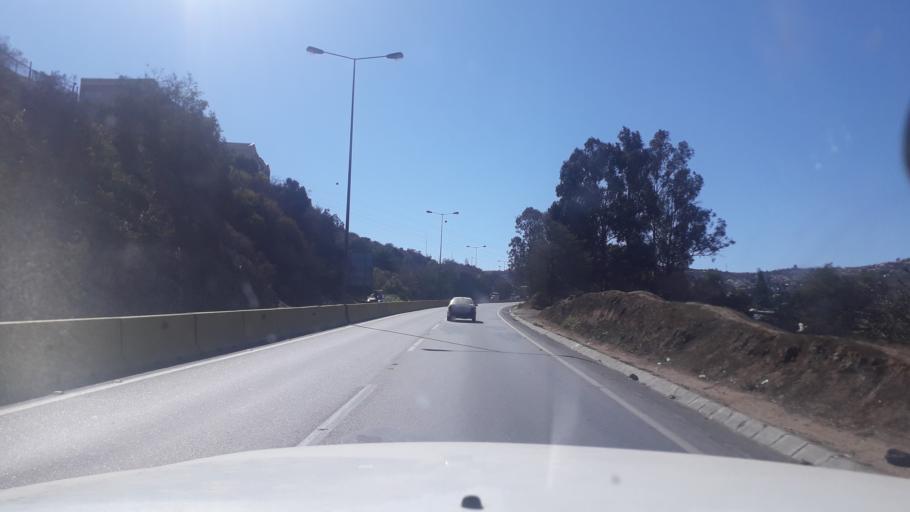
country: CL
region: Valparaiso
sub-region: Provincia de Valparaiso
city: Vina del Mar
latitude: -33.0327
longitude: -71.5008
